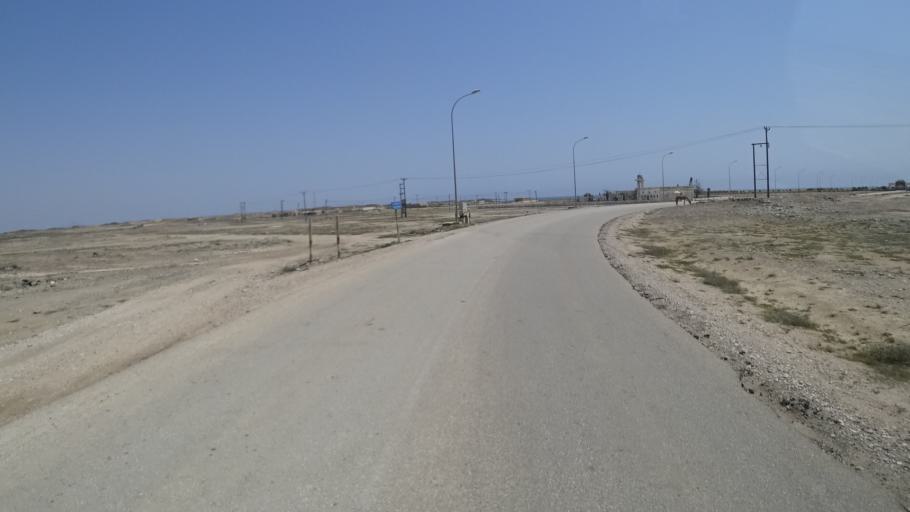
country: OM
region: Zufar
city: Salalah
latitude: 16.9661
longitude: 54.7376
